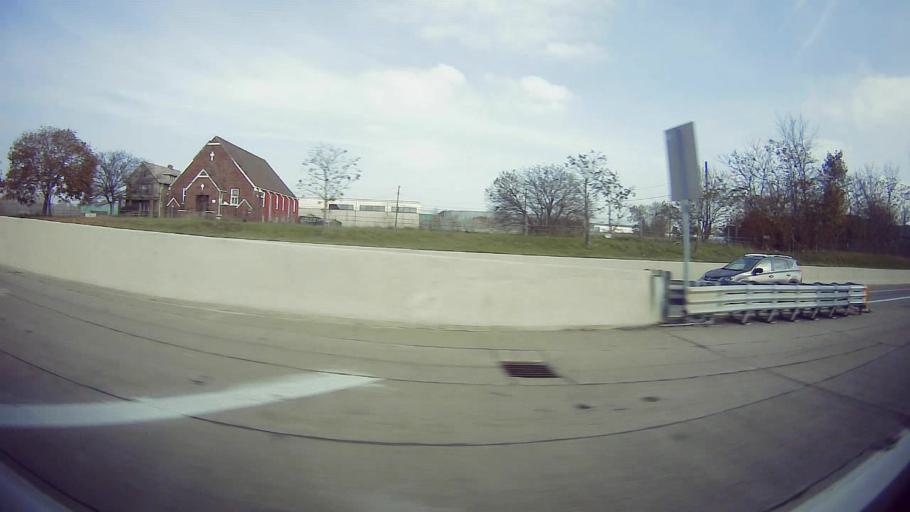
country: US
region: Michigan
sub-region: Wayne County
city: Highland Park
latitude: 42.3969
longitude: -83.1086
